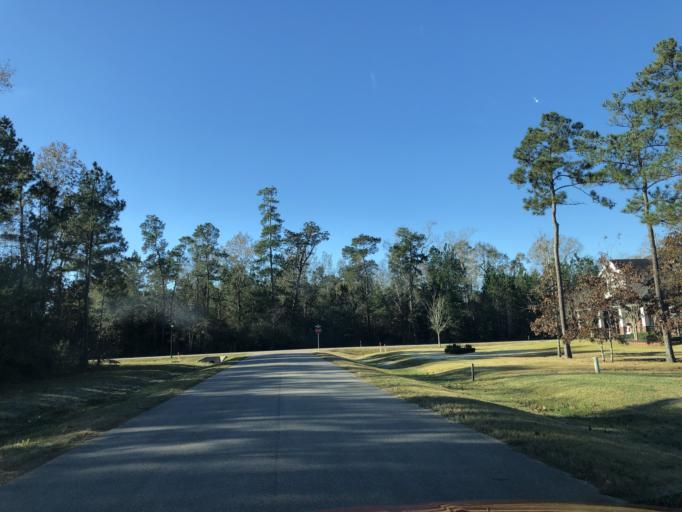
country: US
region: Texas
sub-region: Montgomery County
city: Porter Heights
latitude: 30.0680
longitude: -95.3233
